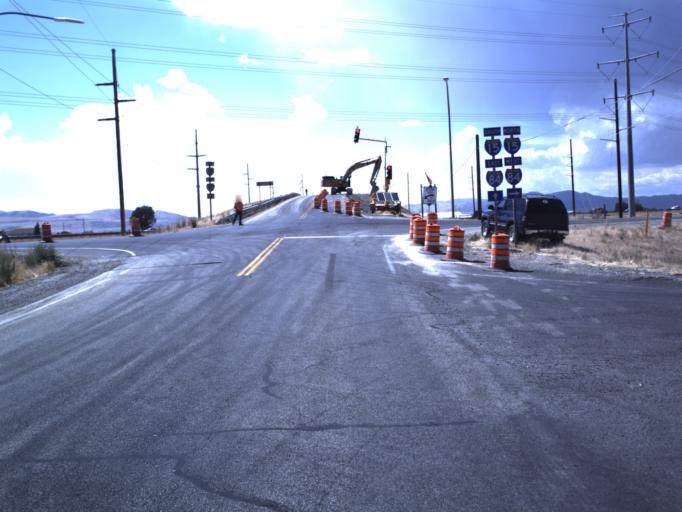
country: US
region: Utah
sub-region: Box Elder County
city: Honeyville
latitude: 41.6350
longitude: -112.0978
